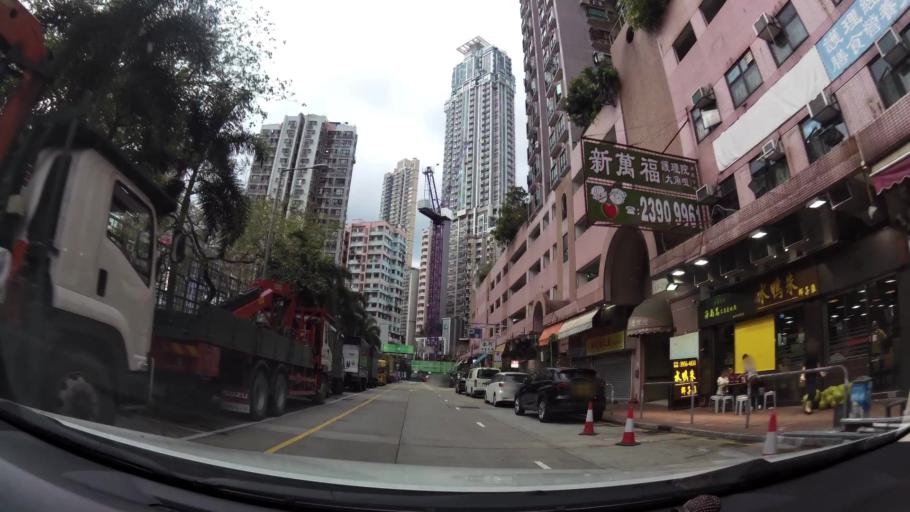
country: HK
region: Sham Shui Po
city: Sham Shui Po
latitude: 22.3193
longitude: 114.1654
